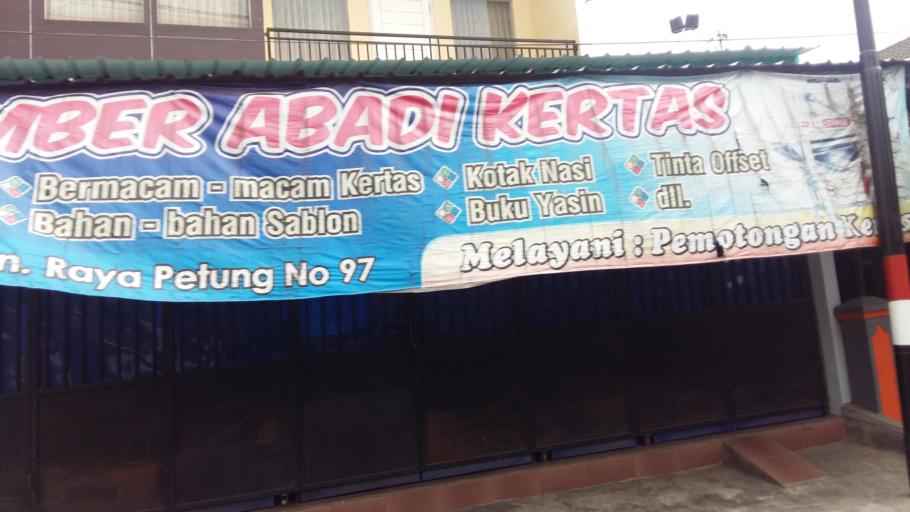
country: ID
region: East Java
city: Krajan
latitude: -8.3173
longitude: 114.2865
